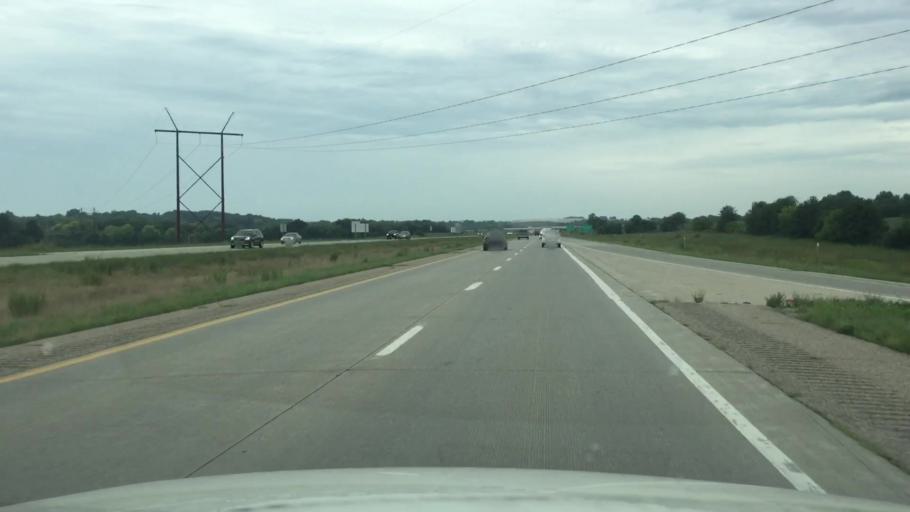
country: US
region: Iowa
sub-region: Warren County
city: Norwalk
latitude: 41.5009
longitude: -93.6304
